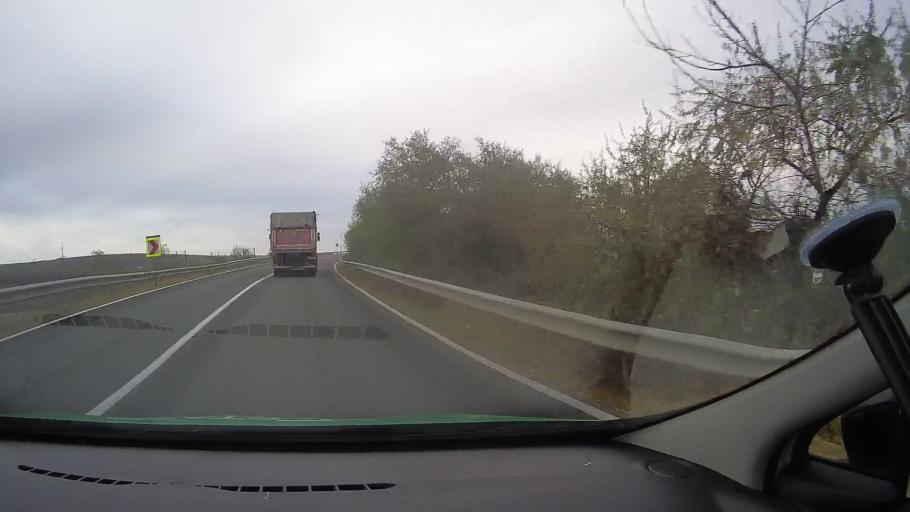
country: RO
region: Constanta
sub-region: Comuna Poarta Alba
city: Poarta Alba
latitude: 44.2148
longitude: 28.3912
